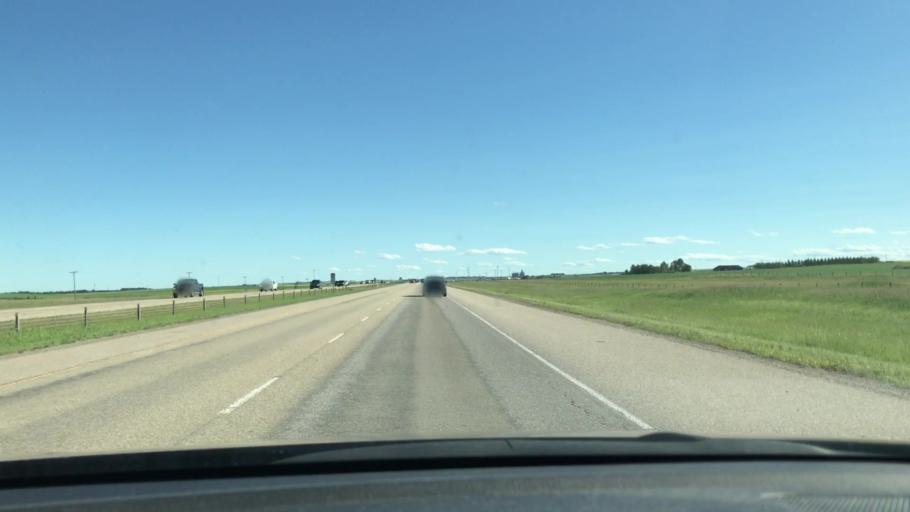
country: CA
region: Alberta
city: Carstairs
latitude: 51.5393
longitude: -114.0254
